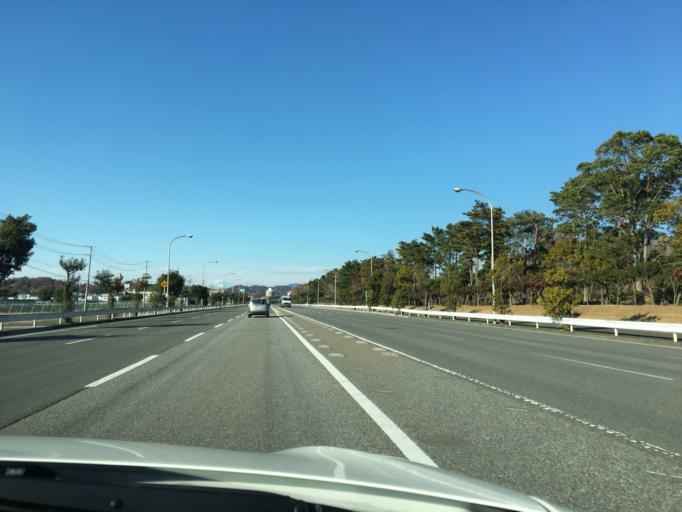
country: JP
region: Fukushima
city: Iwaki
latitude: 36.9329
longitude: 140.8608
